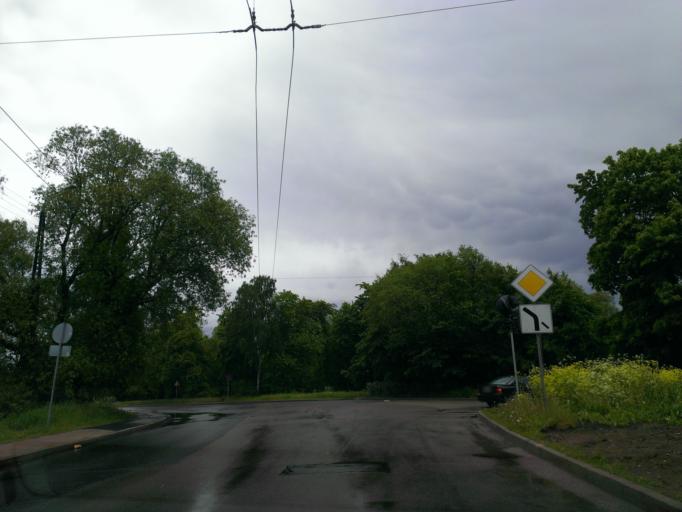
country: LV
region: Riga
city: Riga
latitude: 56.9352
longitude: 24.0977
